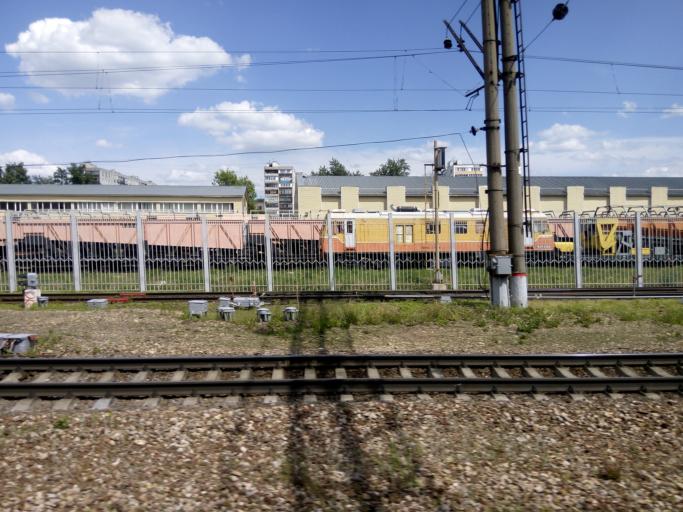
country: RU
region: Moskovskaya
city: Biryulevo Zapadnoye
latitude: 55.5956
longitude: 37.6521
